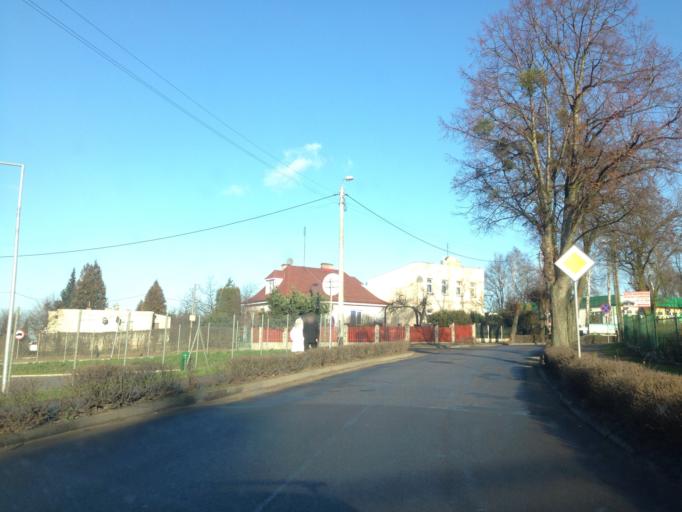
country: PL
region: Kujawsko-Pomorskie
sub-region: Powiat brodnicki
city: Jablonowo Pomorskie
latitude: 53.3907
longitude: 19.1530
